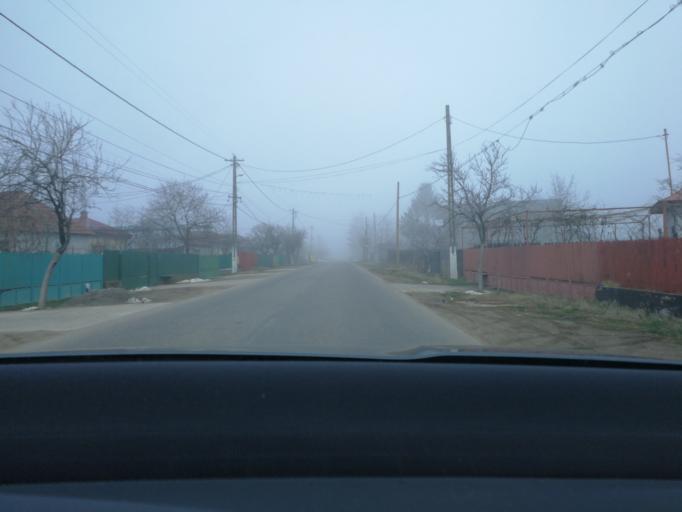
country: RO
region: Prahova
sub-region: Comuna Magureni
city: Lunca Prahovei
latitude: 45.0323
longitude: 25.7659
